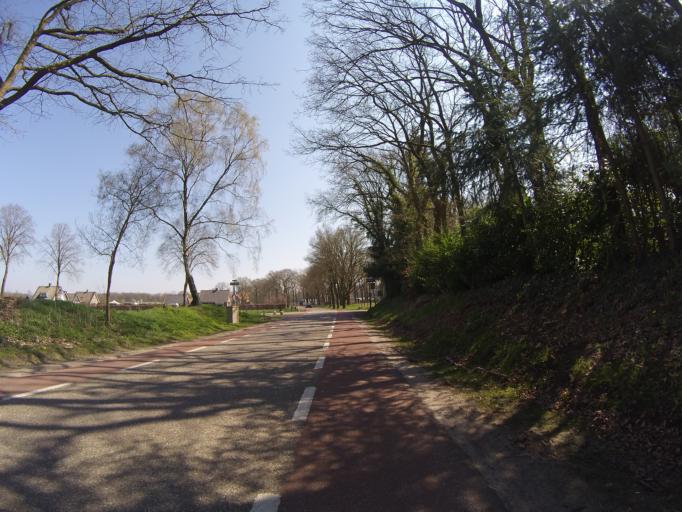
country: NL
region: Utrecht
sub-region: Gemeente Utrechtse Heuvelrug
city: Overberg
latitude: 52.0299
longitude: 5.4977
